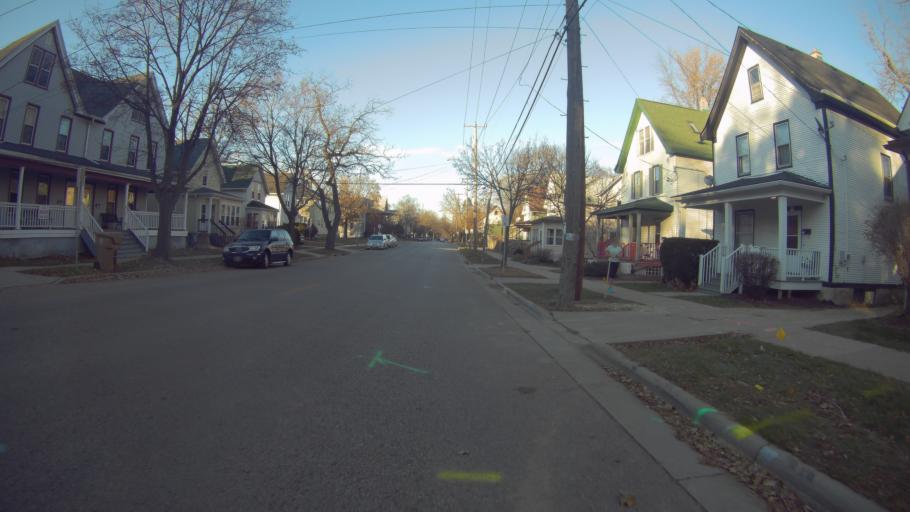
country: US
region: Wisconsin
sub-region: Dane County
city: Madison
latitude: 43.0600
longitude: -89.4040
